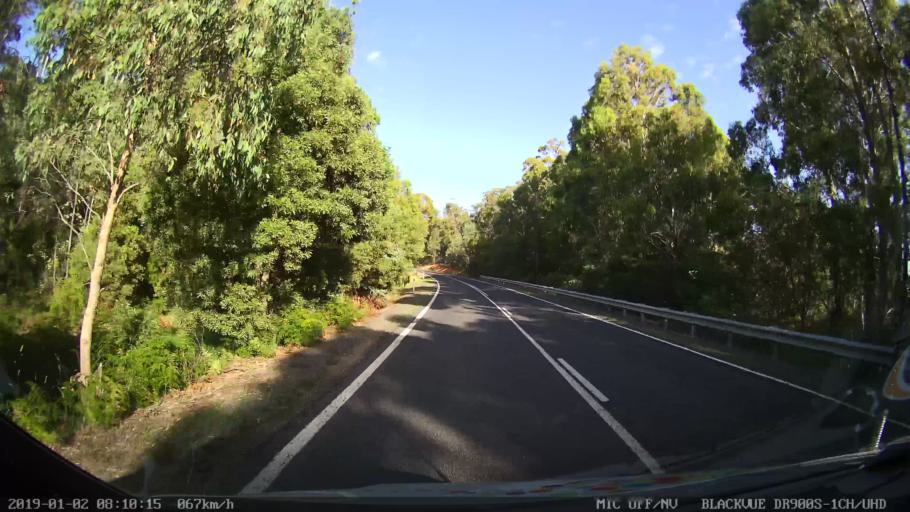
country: AU
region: New South Wales
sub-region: Tumut Shire
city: Tumut
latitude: -35.6002
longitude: 148.3723
